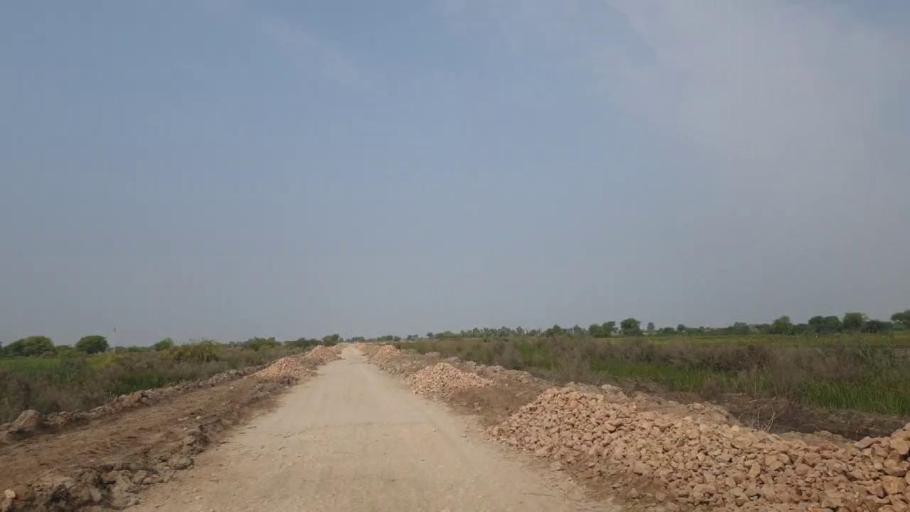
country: PK
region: Sindh
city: Badin
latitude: 24.6086
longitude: 68.7416
